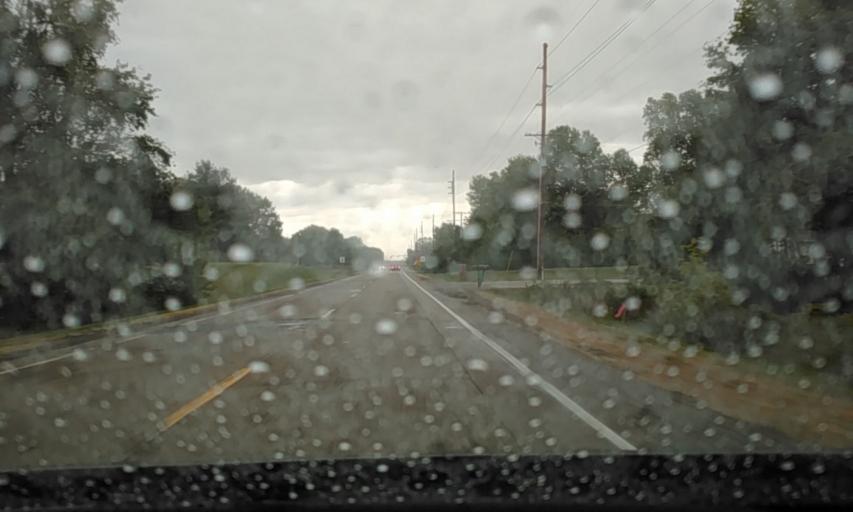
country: US
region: Illinois
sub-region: Madison County
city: Troy
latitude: 38.7177
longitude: -89.8610
